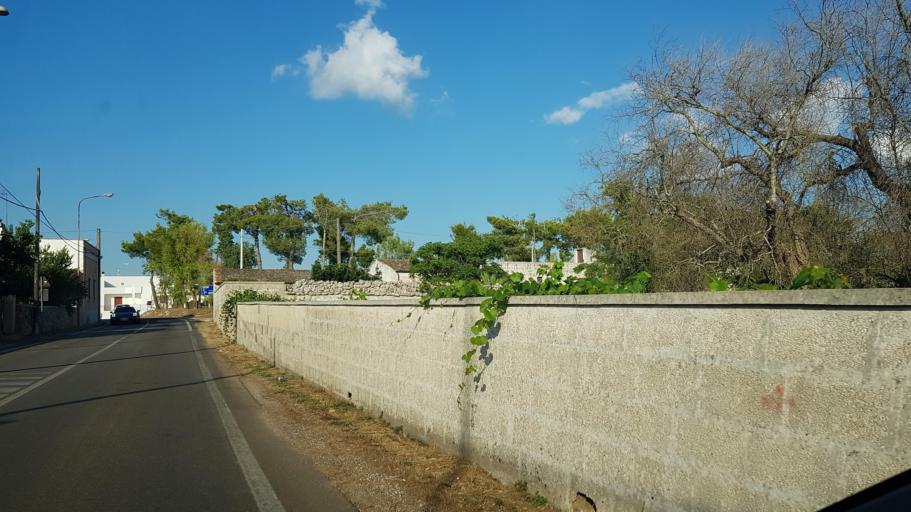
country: IT
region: Apulia
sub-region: Provincia di Lecce
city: Castiglione
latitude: 39.9795
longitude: 18.3422
